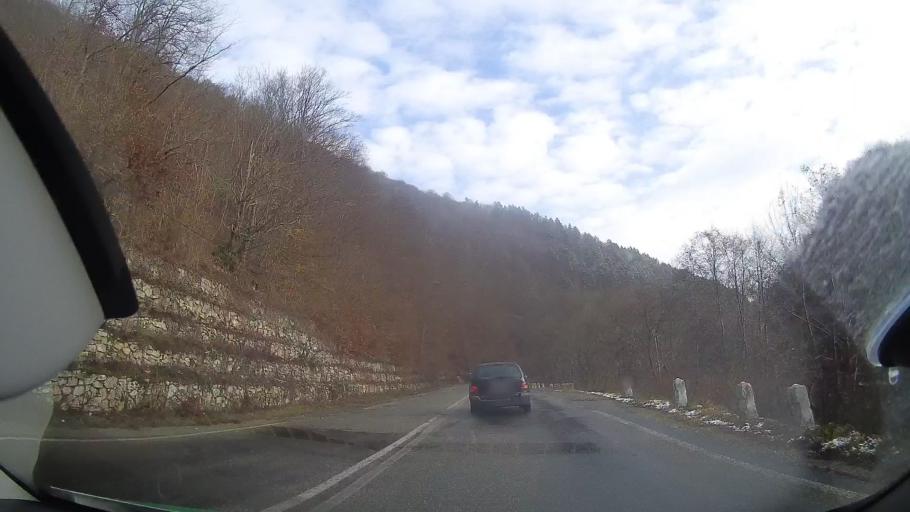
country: RO
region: Alba
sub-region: Oras Baia de Aries
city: Baia de Aries
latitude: 46.3823
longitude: 23.2582
